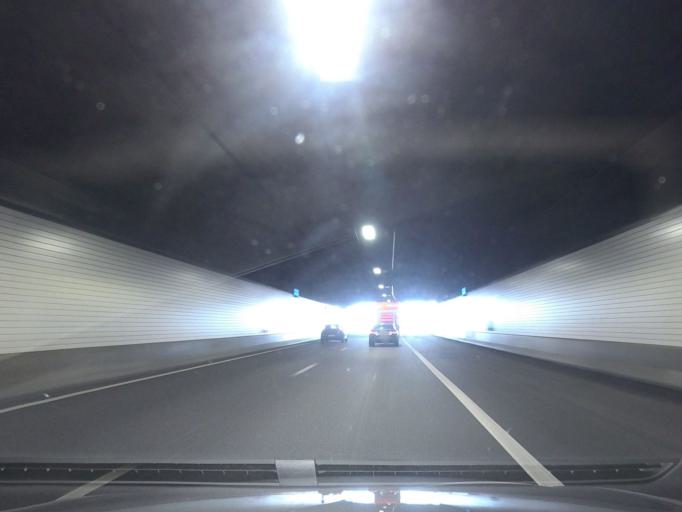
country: NL
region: North Holland
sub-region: Gemeente Velsen
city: Velsen-Zuid
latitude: 52.4603
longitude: 4.6714
